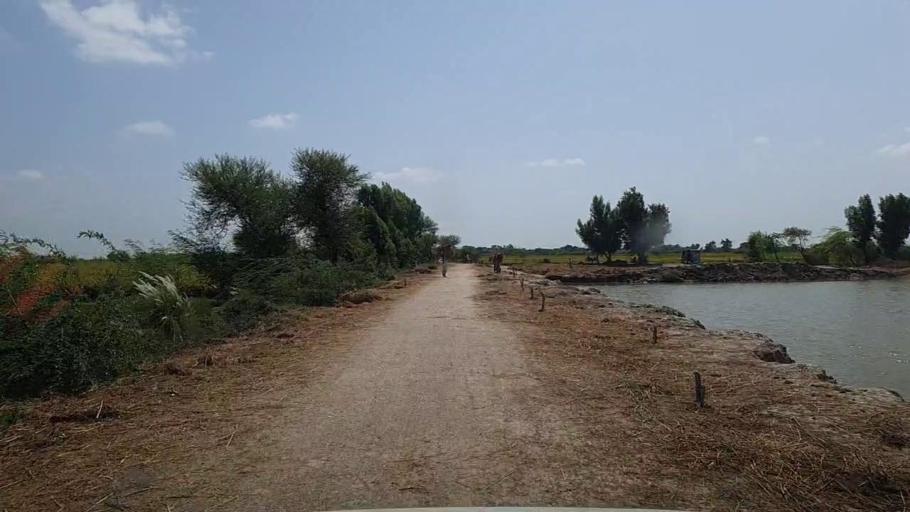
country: PK
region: Sindh
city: Kario
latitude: 24.6386
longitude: 68.5719
